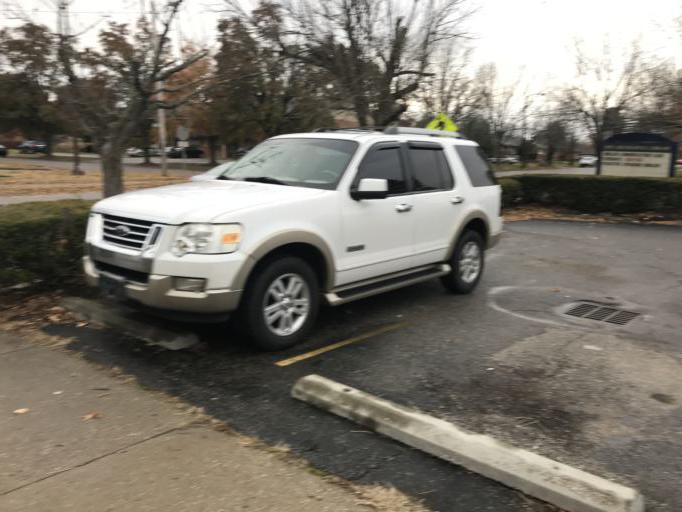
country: US
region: Kentucky
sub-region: Jefferson County
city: West Buechel
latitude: 38.2150
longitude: -85.6554
